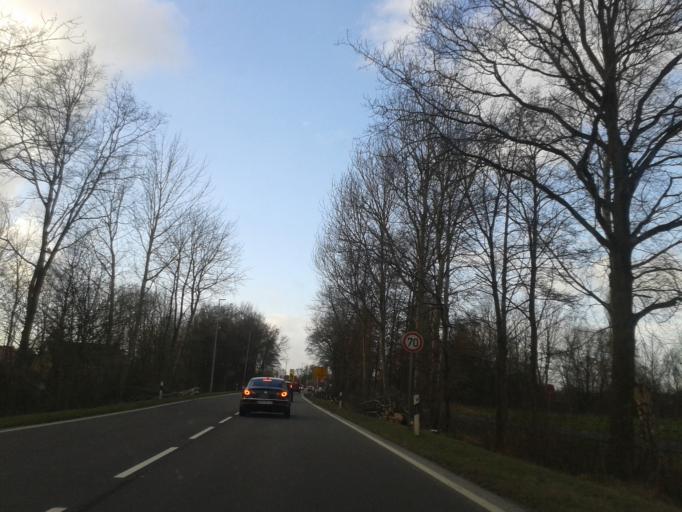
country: DE
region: Lower Saxony
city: Marienhafe
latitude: 53.5276
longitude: 7.2743
